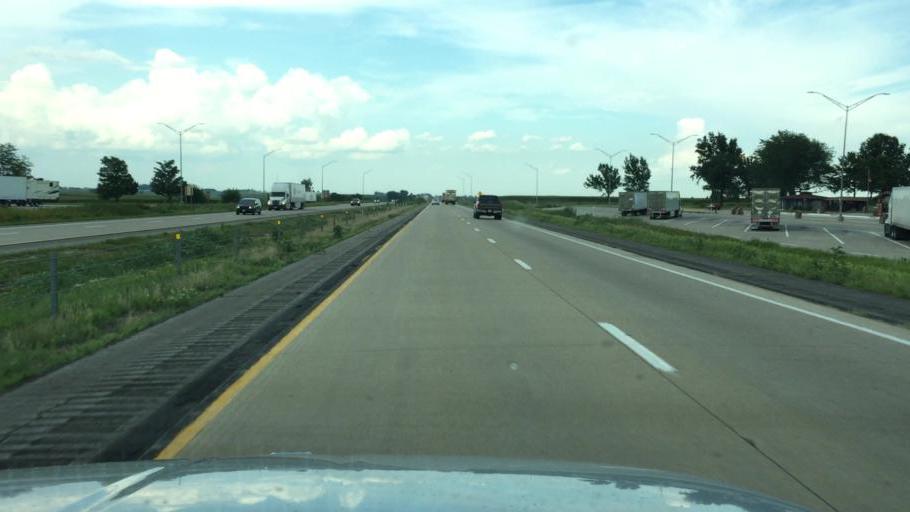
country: US
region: Iowa
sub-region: Iowa County
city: Marengo
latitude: 41.6957
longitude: -92.2321
